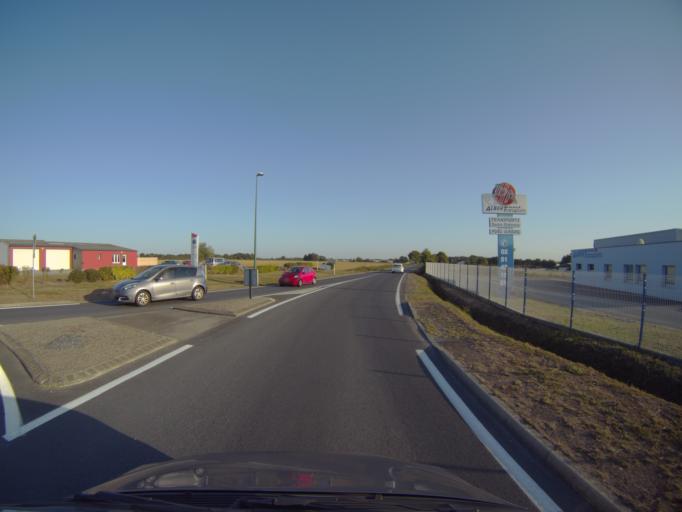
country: FR
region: Pays de la Loire
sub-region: Departement de la Vendee
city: Cugand
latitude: 47.0557
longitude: -1.2541
